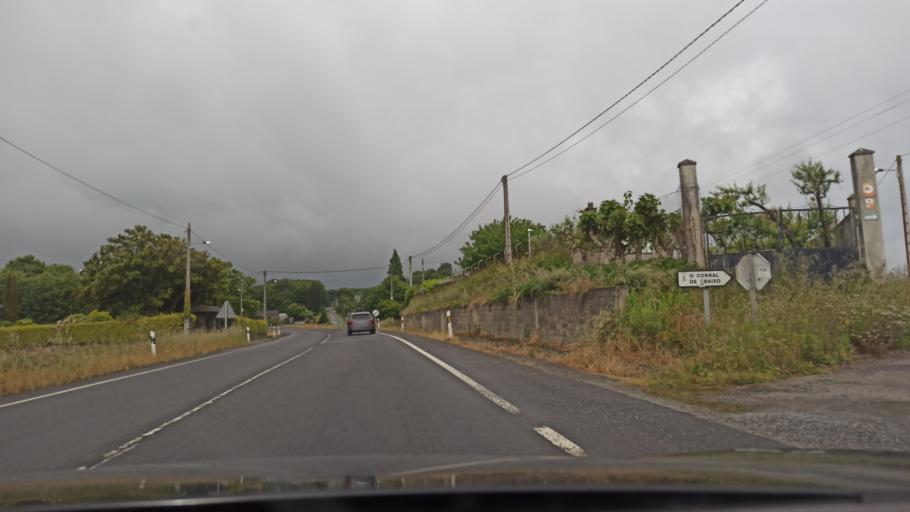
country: ES
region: Galicia
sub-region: Provincia de Lugo
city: Lugo
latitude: 42.9551
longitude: -7.6114
